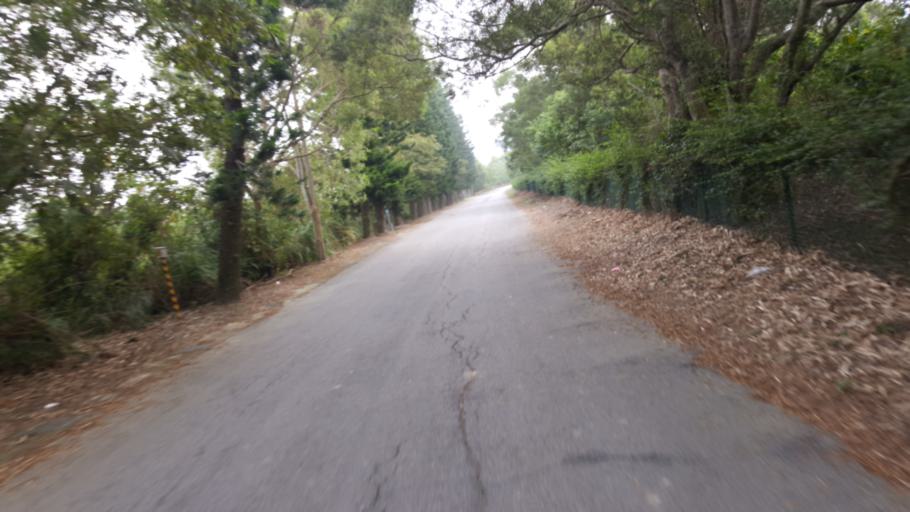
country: TW
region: Taiwan
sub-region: Hsinchu
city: Hsinchu
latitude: 24.7142
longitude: 120.9506
